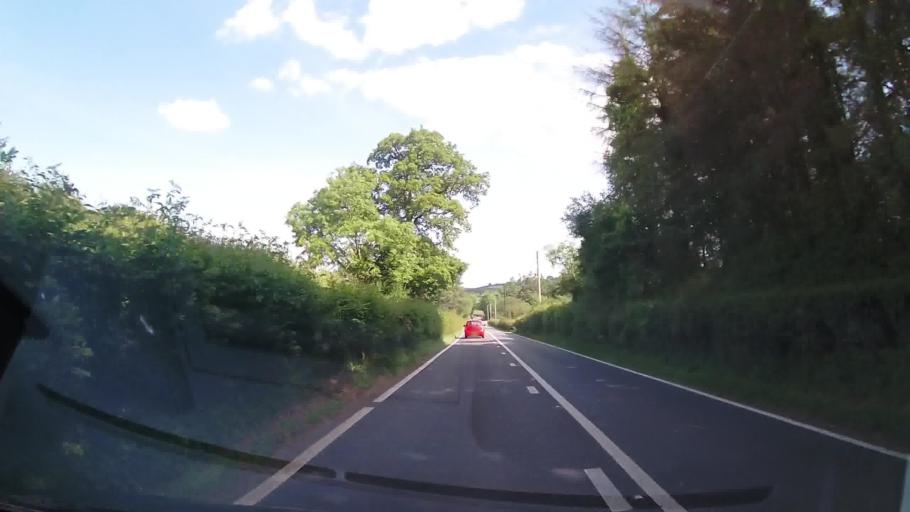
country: GB
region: Wales
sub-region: Sir Powys
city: Llanfyllin
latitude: 52.6691
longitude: -3.3835
